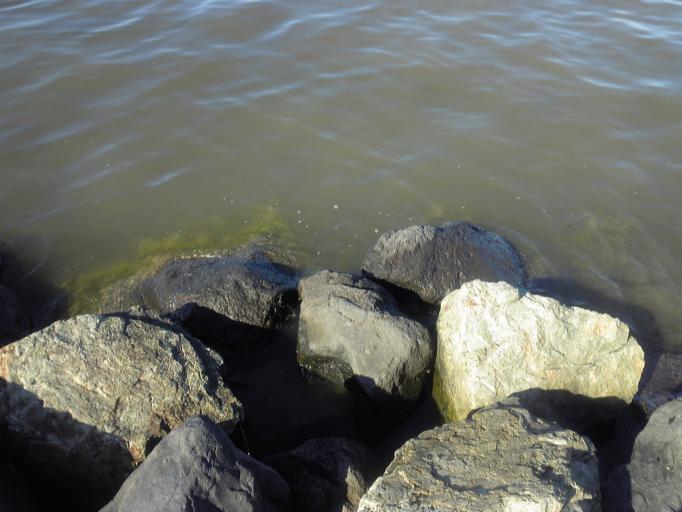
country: JP
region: Hokkaido
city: Makubetsu
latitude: 45.5225
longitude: 141.9367
